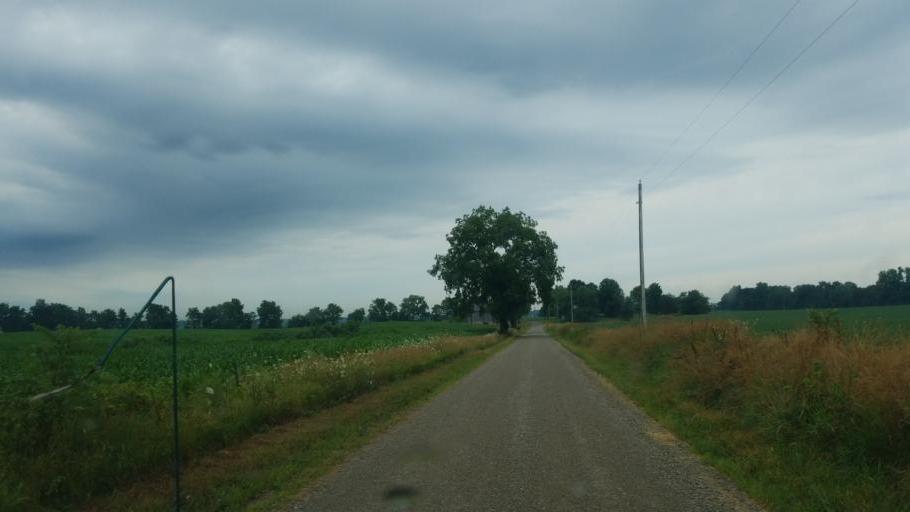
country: US
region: Indiana
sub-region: Steuben County
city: Hamilton
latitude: 41.5034
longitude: -84.9405
